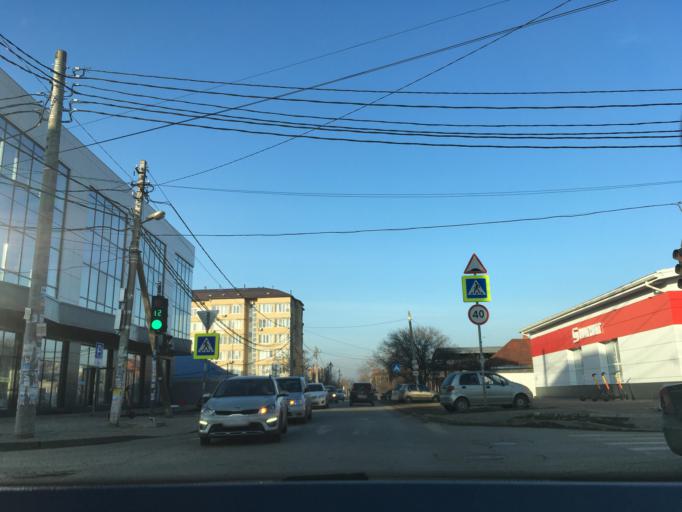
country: RU
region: Krasnodarskiy
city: Krasnodar
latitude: 45.0752
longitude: 39.0210
